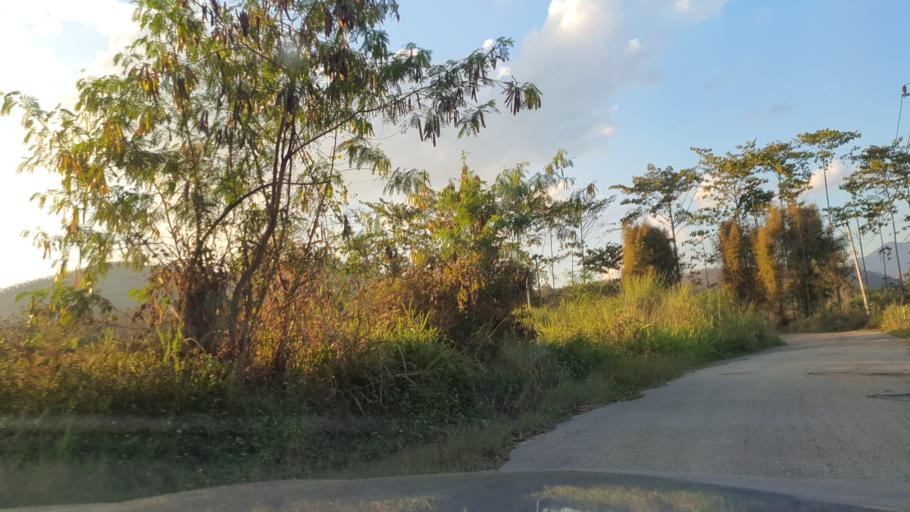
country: TH
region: Chiang Mai
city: Hang Dong
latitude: 18.7328
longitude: 98.8870
